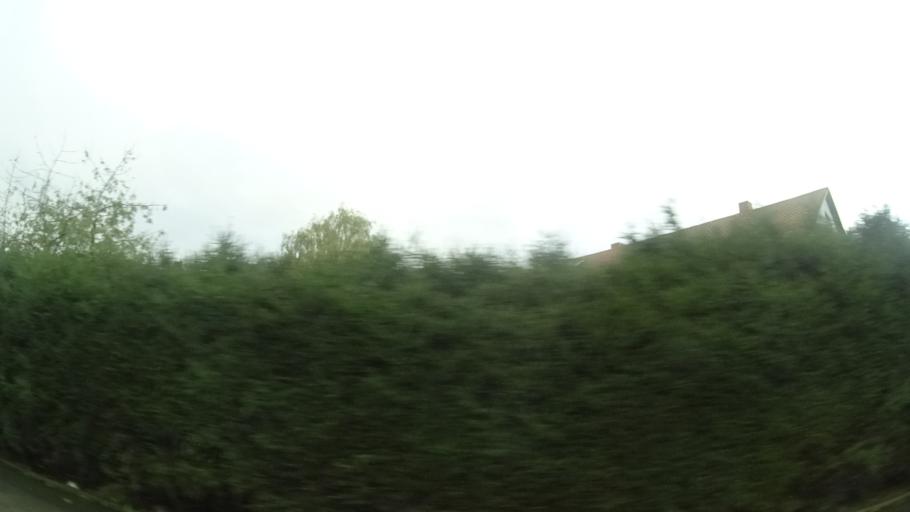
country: DE
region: Hesse
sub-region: Regierungsbezirk Giessen
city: Grebenhain
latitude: 50.4727
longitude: 9.3838
